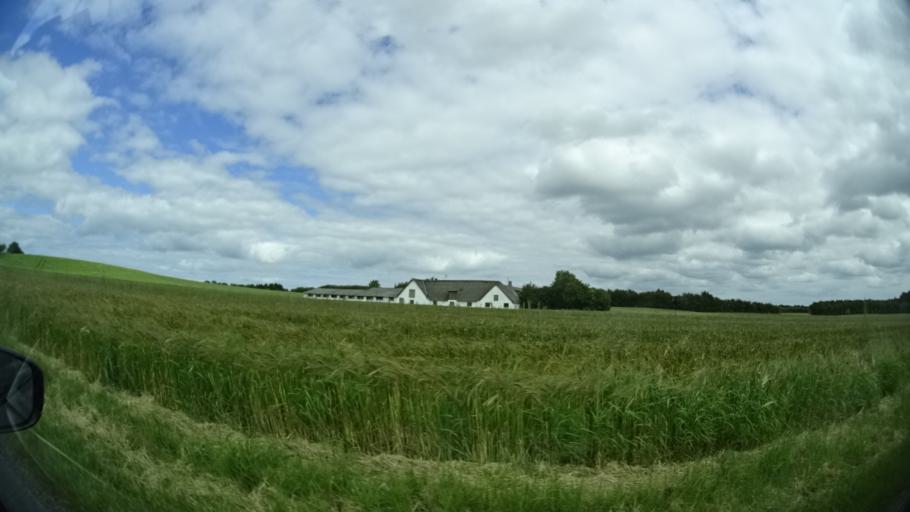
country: DK
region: Central Jutland
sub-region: Norddjurs Kommune
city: Grenaa
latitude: 56.5139
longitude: 10.7284
